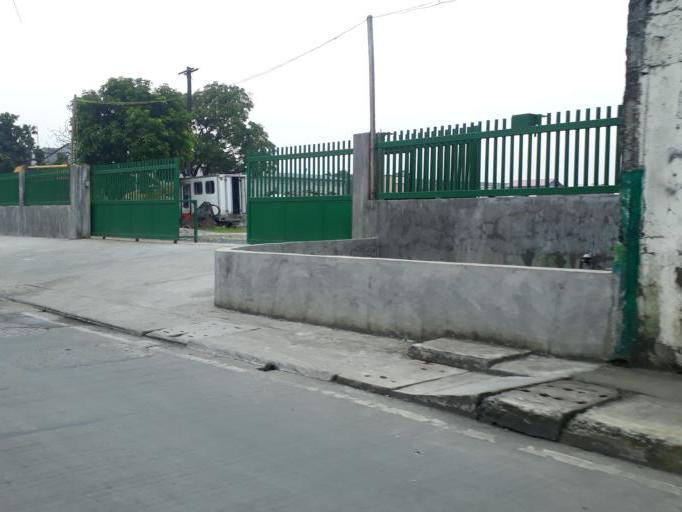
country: PH
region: Calabarzon
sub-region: Province of Rizal
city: Valenzuela
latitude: 14.7014
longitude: 120.9565
